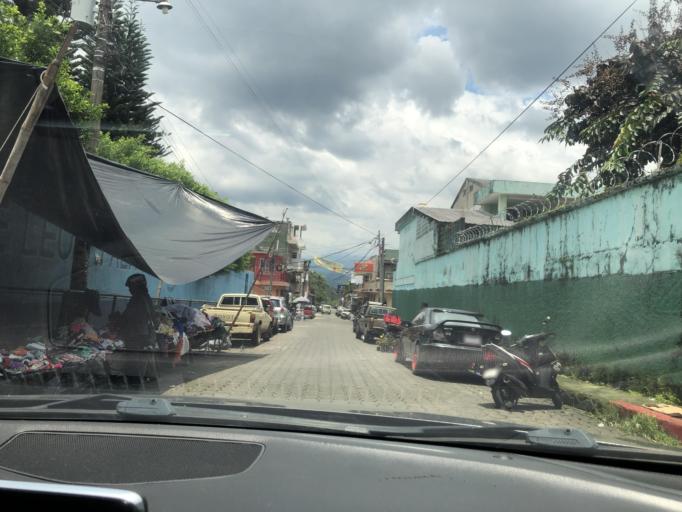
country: GT
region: Quetzaltenango
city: Coatepeque
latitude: 14.7057
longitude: -91.8643
